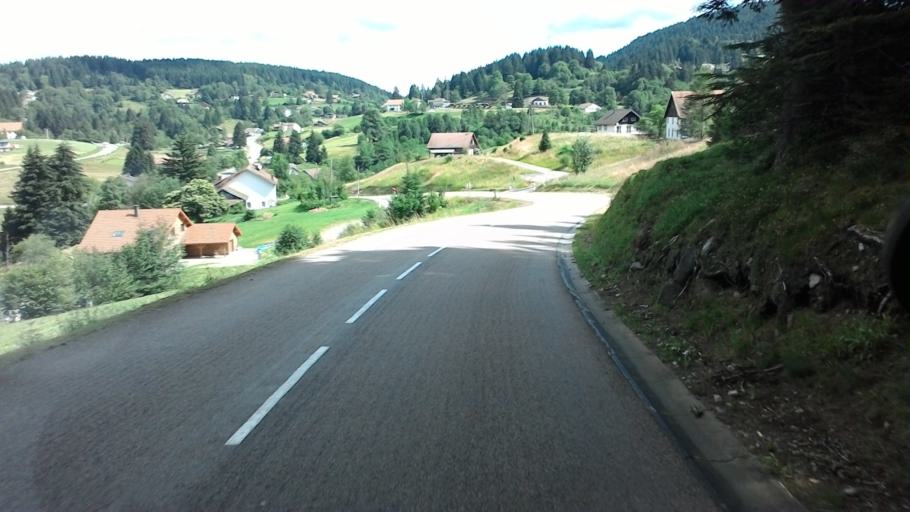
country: FR
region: Lorraine
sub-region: Departement des Vosges
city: Gerardmer
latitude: 48.0414
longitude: 6.8671
